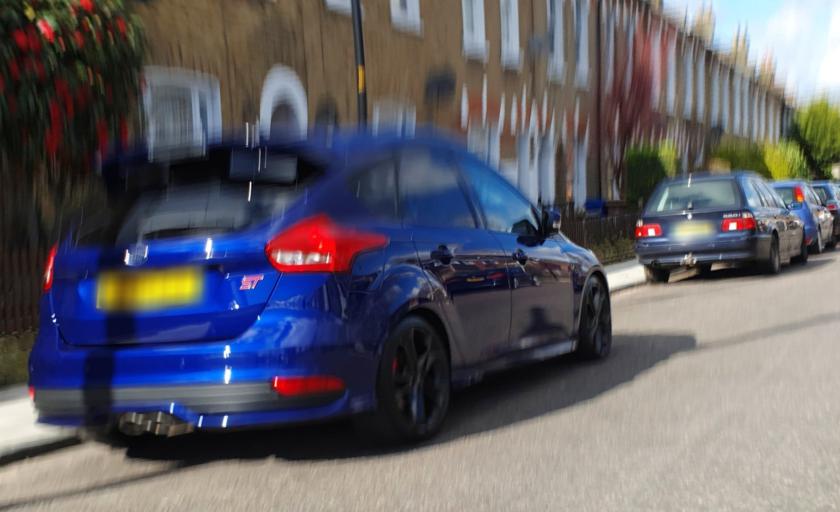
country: GB
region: England
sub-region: Greater London
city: Camberwell
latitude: 51.4666
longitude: -0.0584
